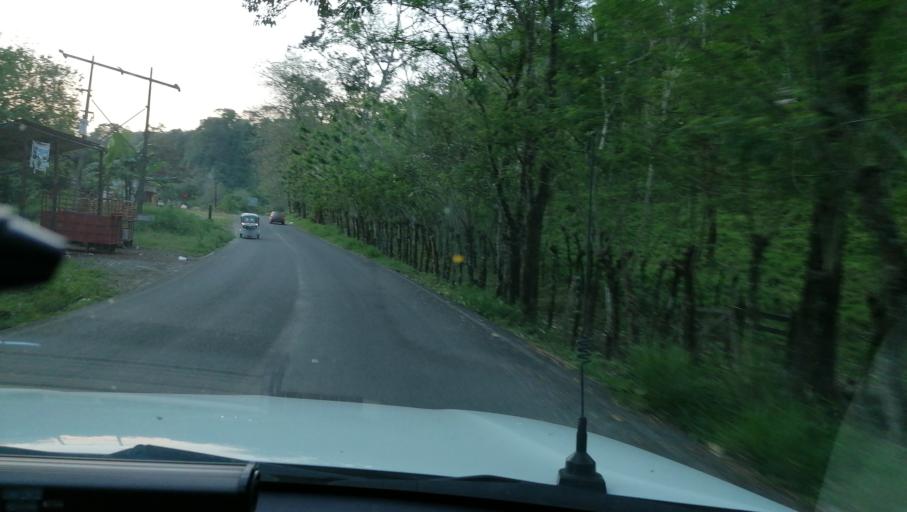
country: MX
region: Chiapas
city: Ostuacan
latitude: 17.4161
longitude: -93.3393
